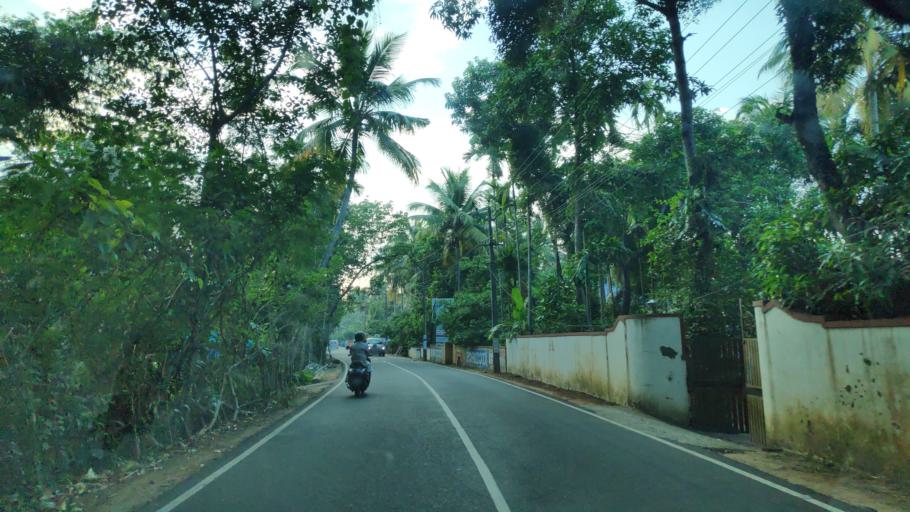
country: IN
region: Kerala
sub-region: Alappuzha
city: Shertallai
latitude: 9.6787
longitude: 76.3887
